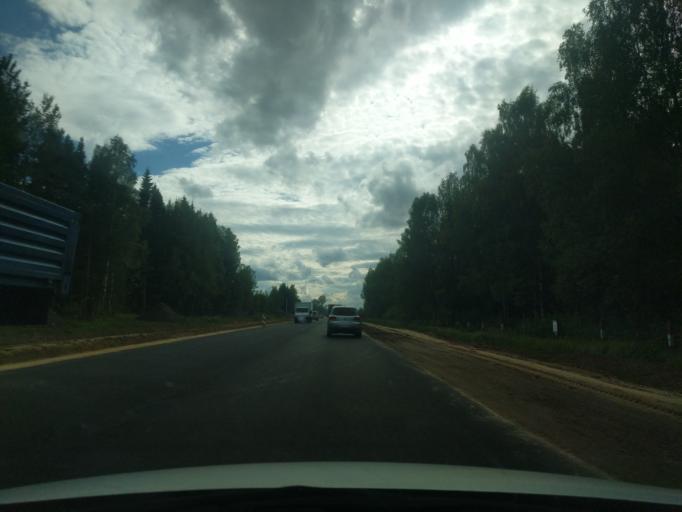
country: RU
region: Jaroslavl
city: Levashevo
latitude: 57.6618
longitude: 40.5697
